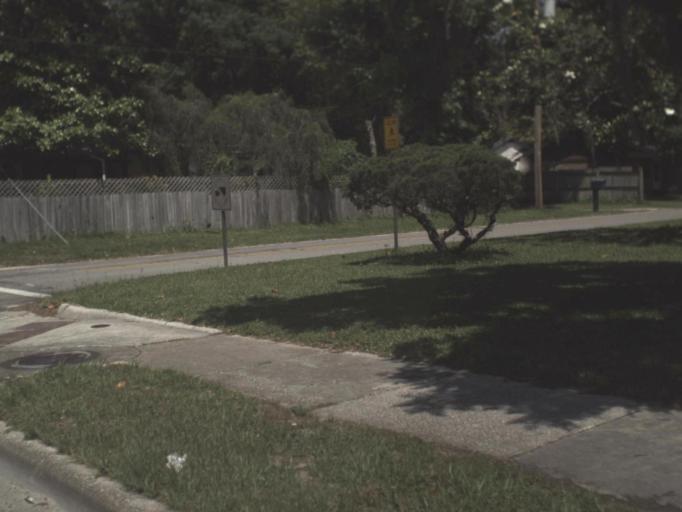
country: US
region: Florida
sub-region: Bradford County
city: Starke
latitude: 29.9448
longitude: -82.1161
